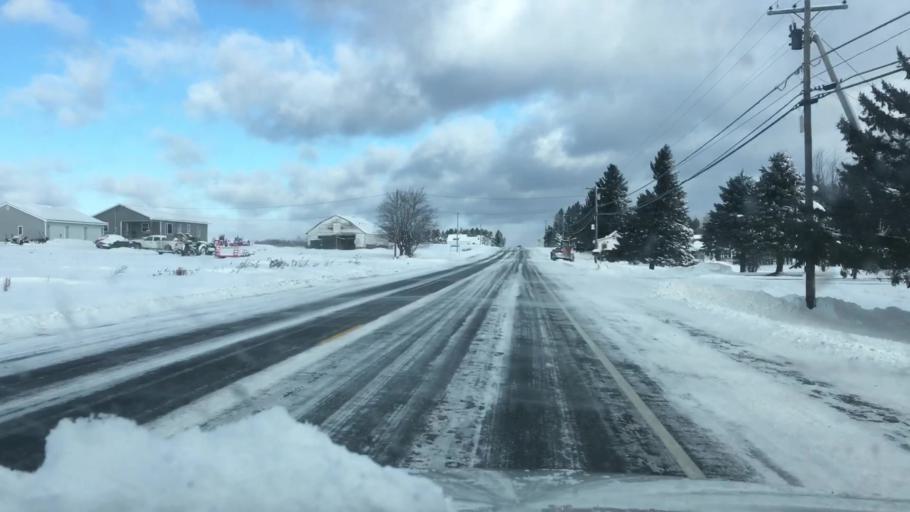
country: US
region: Maine
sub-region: Aroostook County
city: Caribou
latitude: 46.9077
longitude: -68.0164
